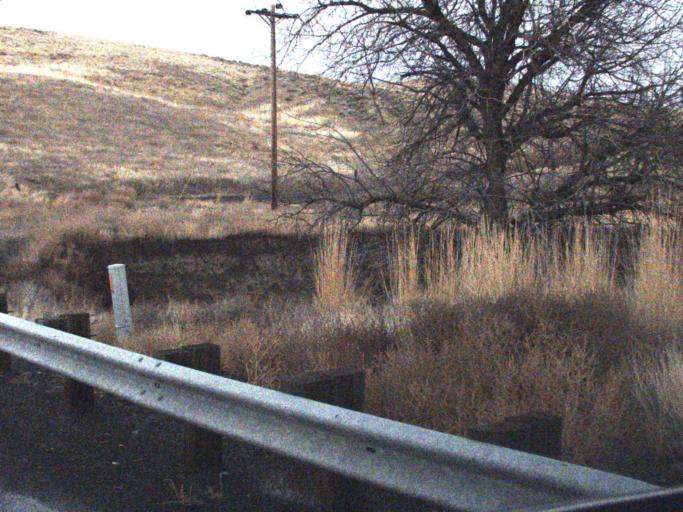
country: US
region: Washington
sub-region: Columbia County
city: Dayton
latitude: 46.5120
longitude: -117.9730
